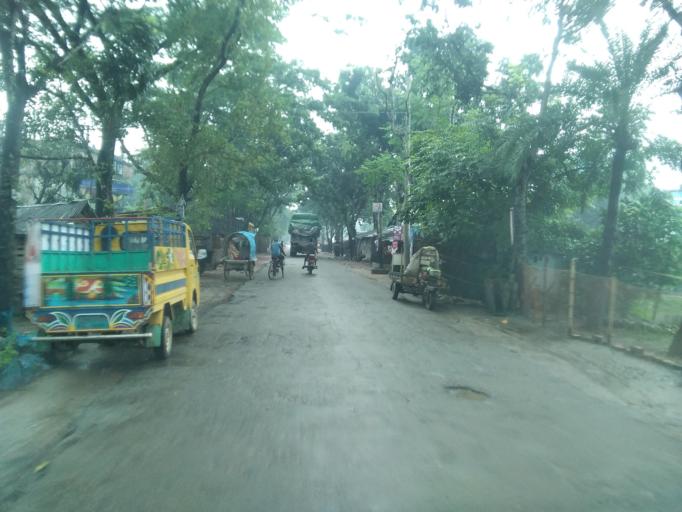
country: IN
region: West Bengal
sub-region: North 24 Parganas
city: Taki
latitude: 22.3496
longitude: 89.1032
